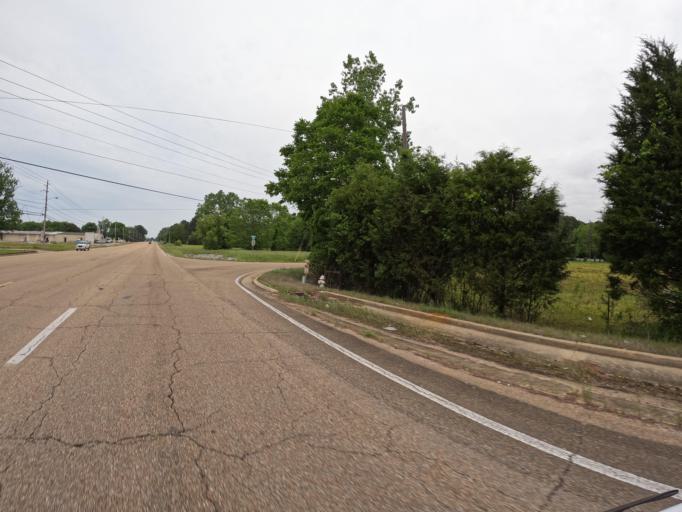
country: US
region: Mississippi
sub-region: Lee County
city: Tupelo
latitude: 34.2925
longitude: -88.7553
